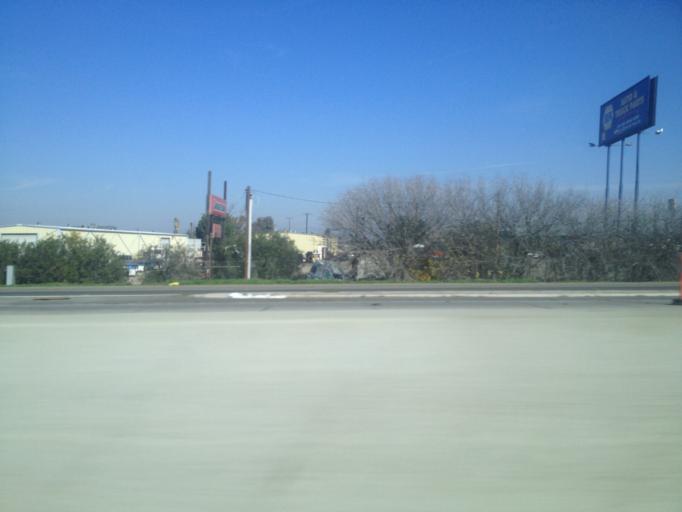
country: US
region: California
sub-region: Fresno County
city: Kingsburg
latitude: 36.5202
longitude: -119.5643
